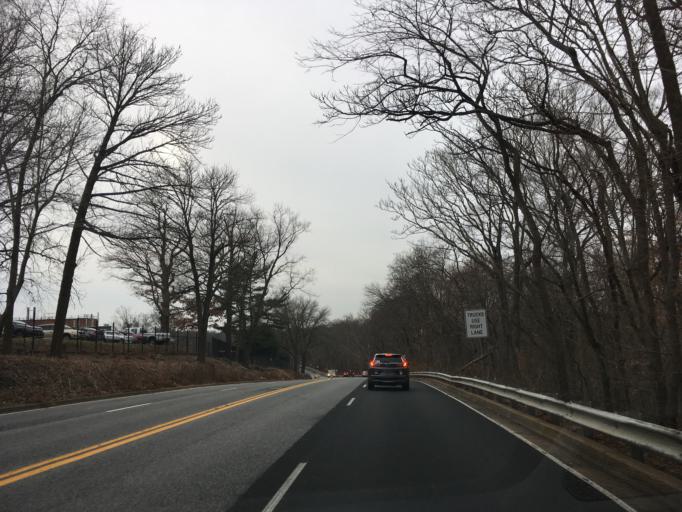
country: US
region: Delaware
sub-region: New Castle County
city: Greenville
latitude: 39.7758
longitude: -75.5727
